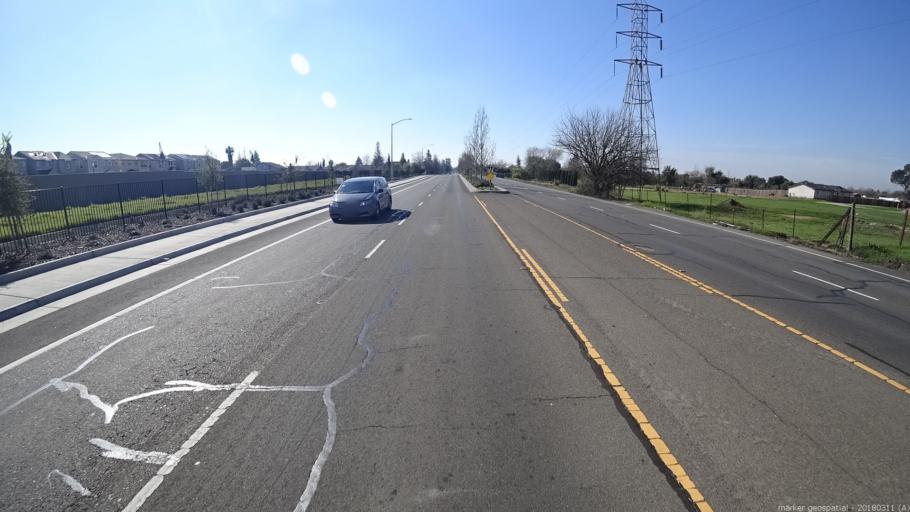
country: US
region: California
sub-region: Sacramento County
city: Florin
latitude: 38.4720
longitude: -121.4087
